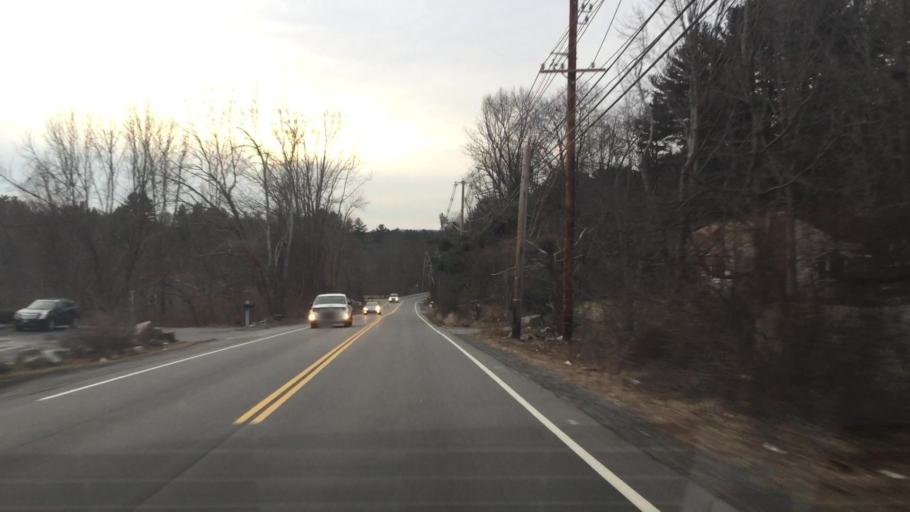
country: US
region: New Hampshire
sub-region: Hillsborough County
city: Pelham
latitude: 42.7450
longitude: -71.2851
